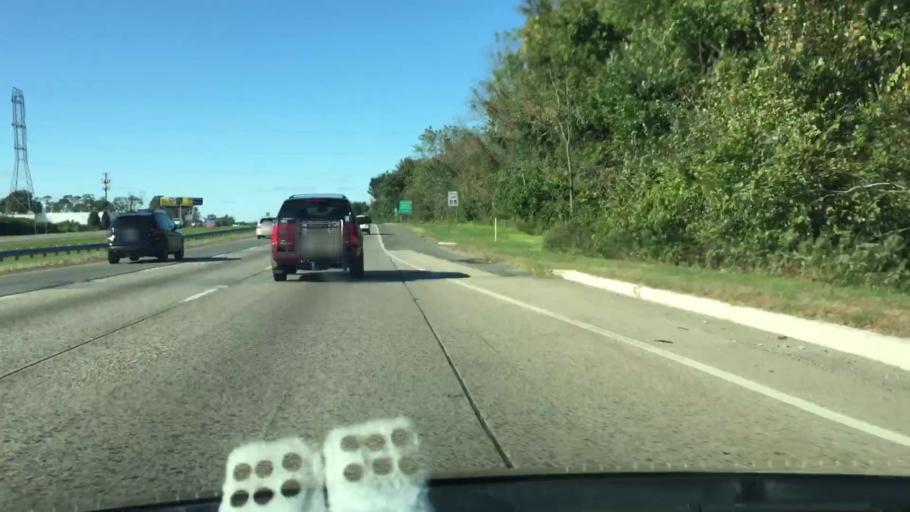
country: US
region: New Jersey
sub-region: Camden County
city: Blackwood
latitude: 39.8062
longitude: -75.0574
